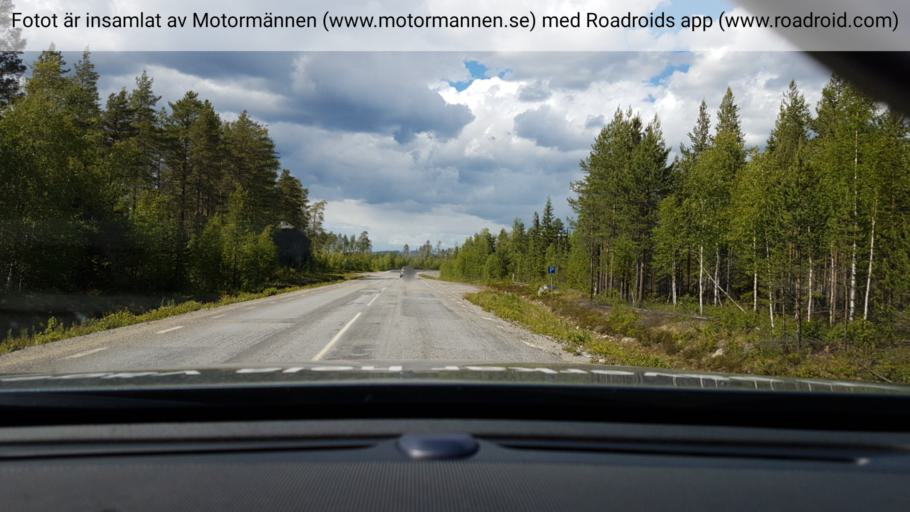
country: SE
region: Vaesterbotten
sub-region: Lycksele Kommun
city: Lycksele
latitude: 63.9783
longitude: 18.4922
